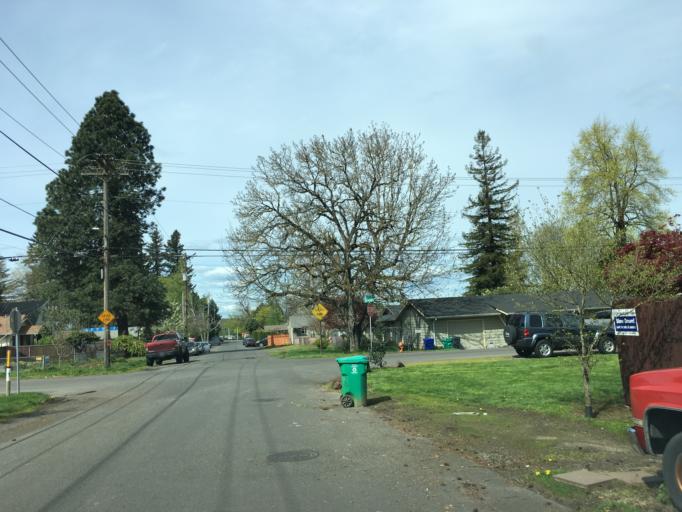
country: US
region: Oregon
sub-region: Multnomah County
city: Lents
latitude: 45.5569
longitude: -122.5608
